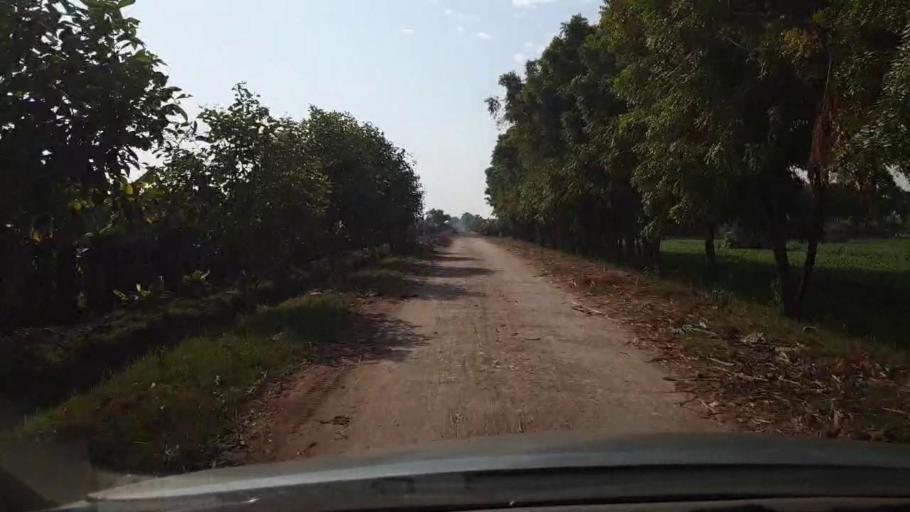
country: PK
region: Sindh
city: Matiari
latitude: 25.5509
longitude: 68.5159
